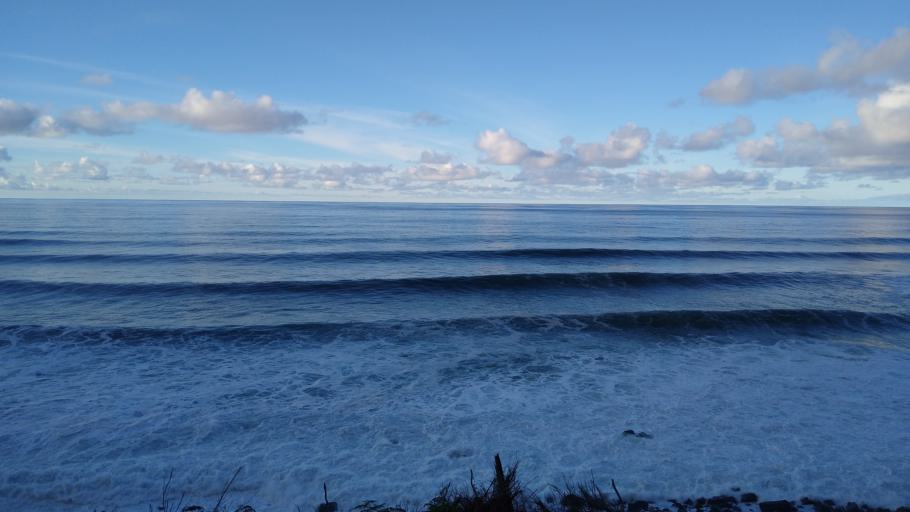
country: PT
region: Madeira
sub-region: Santana
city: Santana
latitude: 32.8327
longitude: -16.9211
